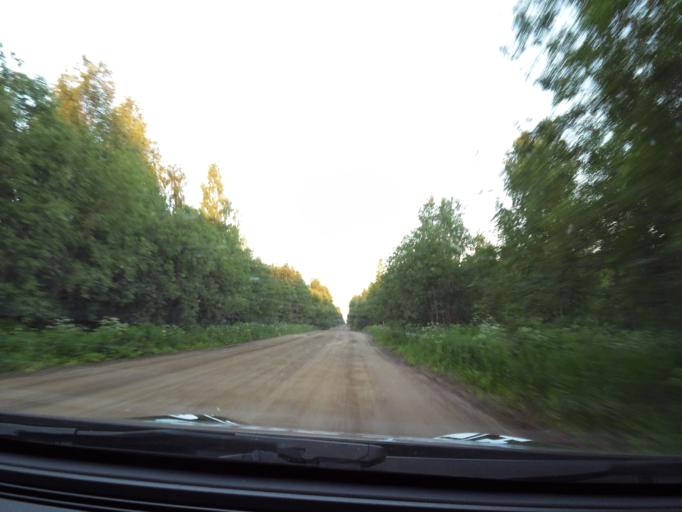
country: RU
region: Leningrad
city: Voznesen'ye
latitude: 60.9008
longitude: 35.5055
